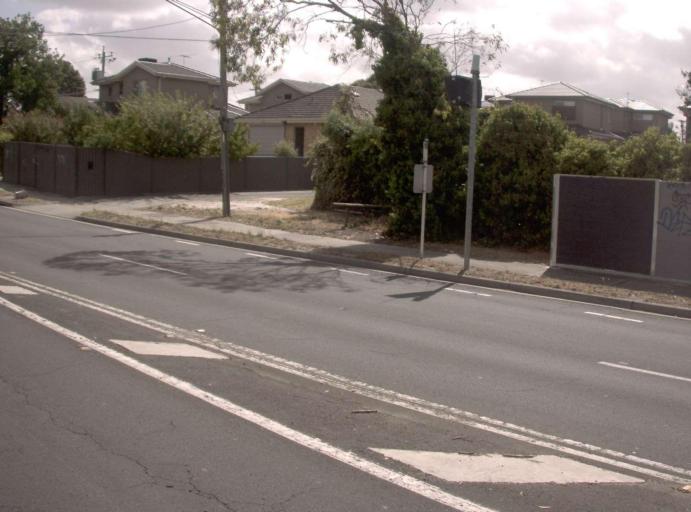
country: AU
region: Victoria
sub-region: Monash
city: Chadstone
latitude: -37.8855
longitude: 145.1084
